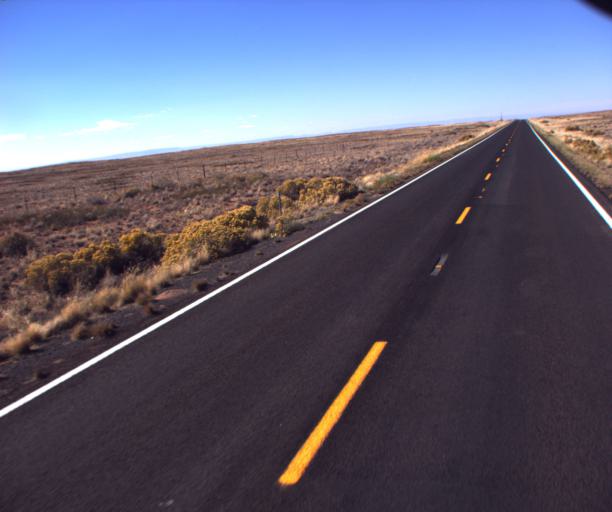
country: US
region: Arizona
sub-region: Coconino County
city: Tuba City
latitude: 35.9777
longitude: -110.9806
